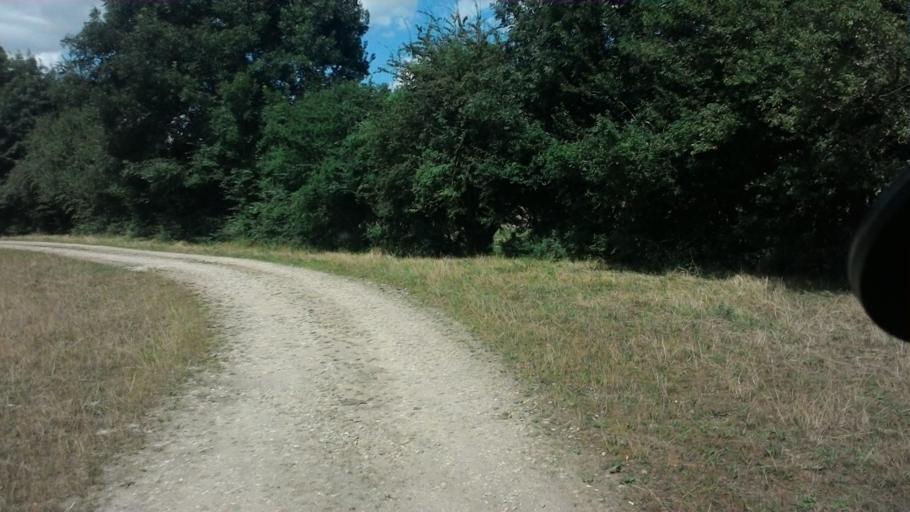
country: FR
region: Bourgogne
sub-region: Departement de la Cote-d'Or
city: Seurre
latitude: 46.9337
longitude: 5.1567
